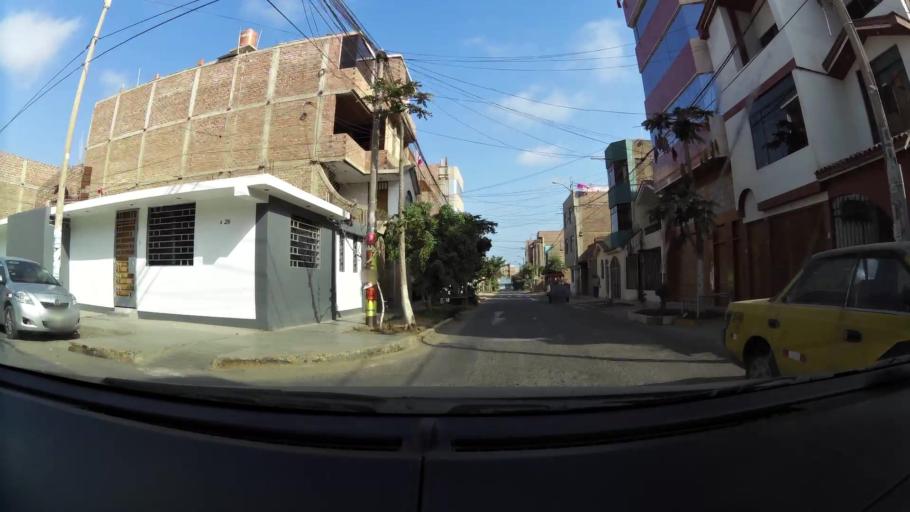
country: PE
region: La Libertad
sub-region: Provincia de Trujillo
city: Trujillo
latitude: -8.1107
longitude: -79.0091
